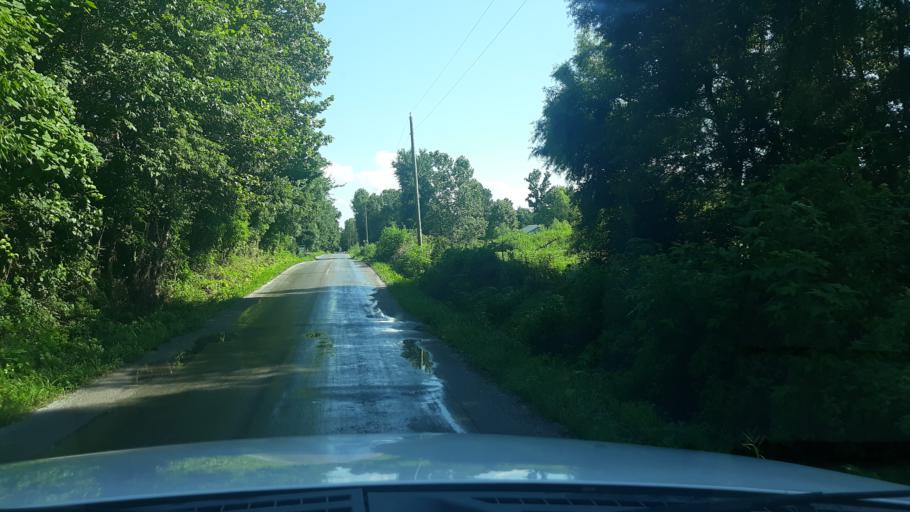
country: US
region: Illinois
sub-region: Saline County
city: Harrisburg
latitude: 37.8621
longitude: -88.5815
